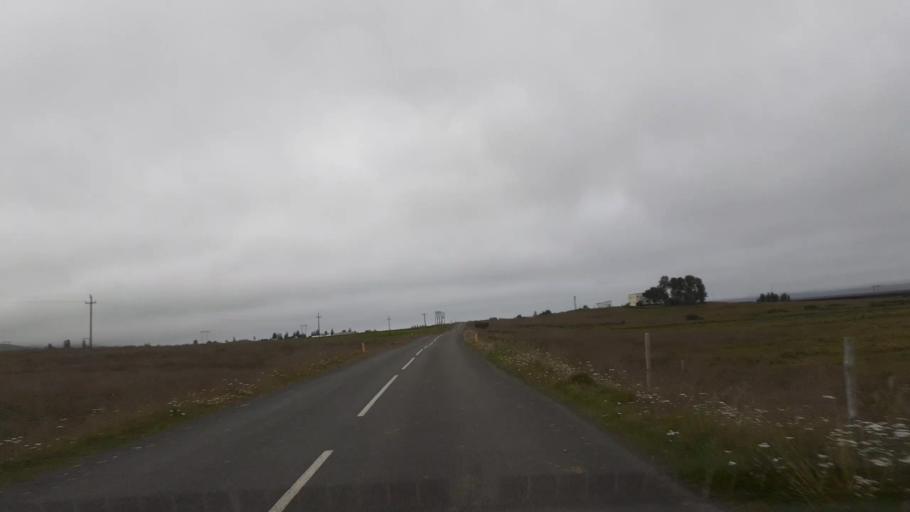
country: IS
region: Northeast
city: Dalvik
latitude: 65.9583
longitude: -18.5470
